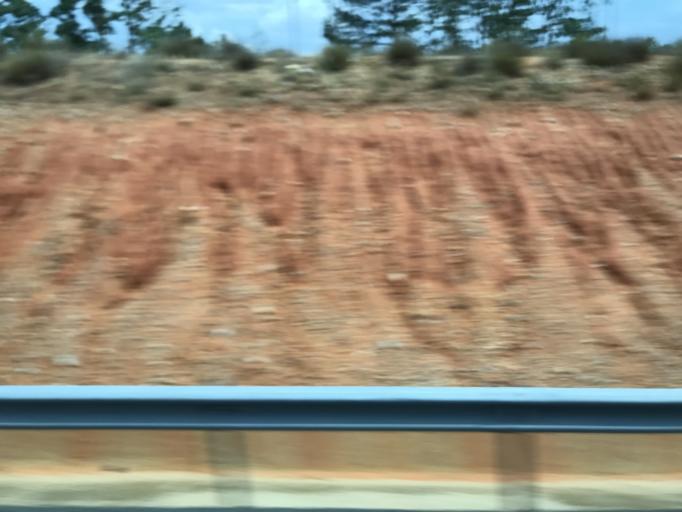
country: ES
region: Castille and Leon
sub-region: Provincia de Segovia
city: Fresno de la Fuente
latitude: 41.4093
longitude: -3.6552
